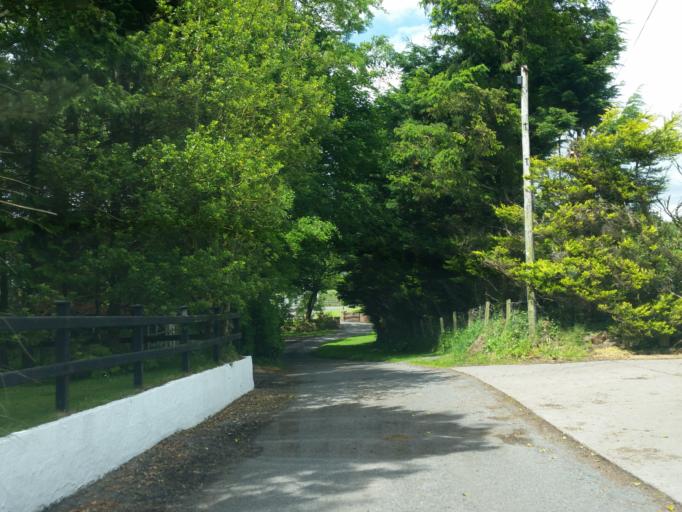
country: GB
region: Northern Ireland
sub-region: Omagh District
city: Omagh
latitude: 54.5532
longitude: -7.0854
